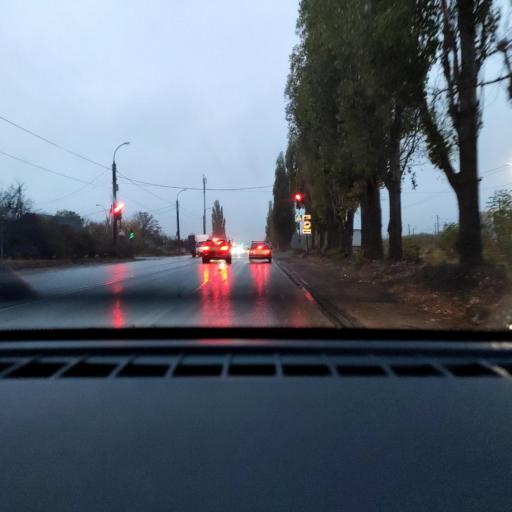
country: RU
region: Voronezj
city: Maslovka
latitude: 51.6176
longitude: 39.2584
